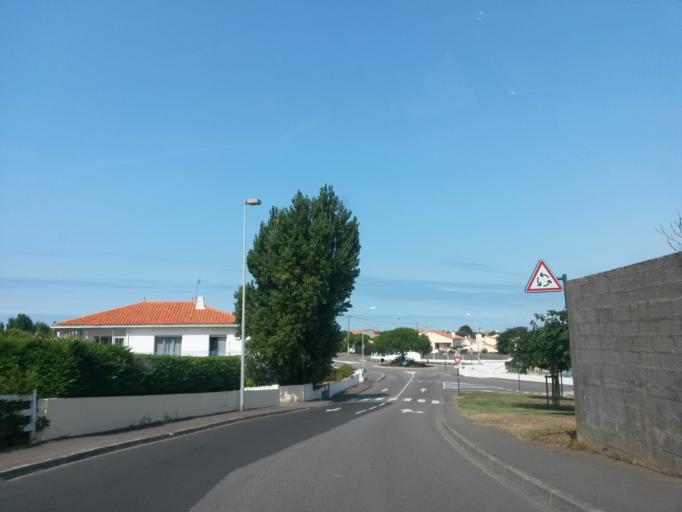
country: FR
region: Pays de la Loire
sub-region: Departement de la Vendee
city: Les Sables-d'Olonne
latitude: 46.5011
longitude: -1.8048
